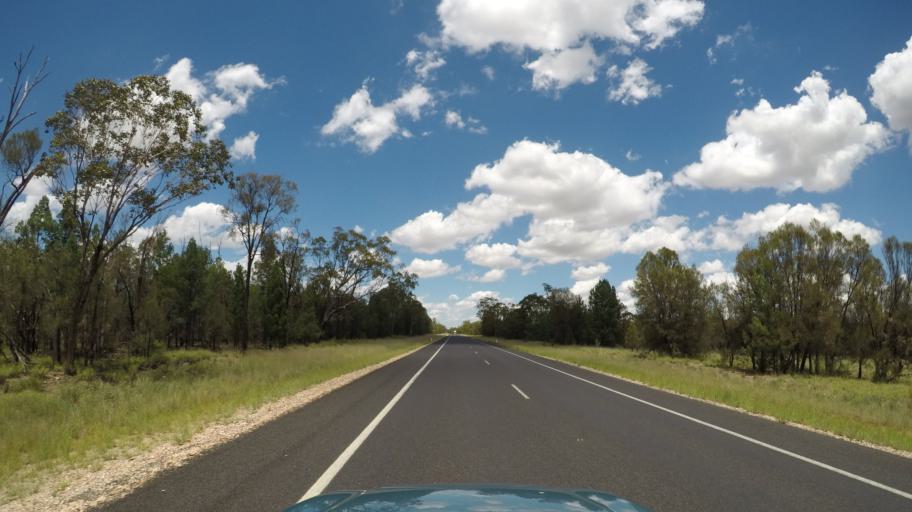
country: AU
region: Queensland
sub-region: Goondiwindi
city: Goondiwindi
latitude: -28.0678
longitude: 150.7556
